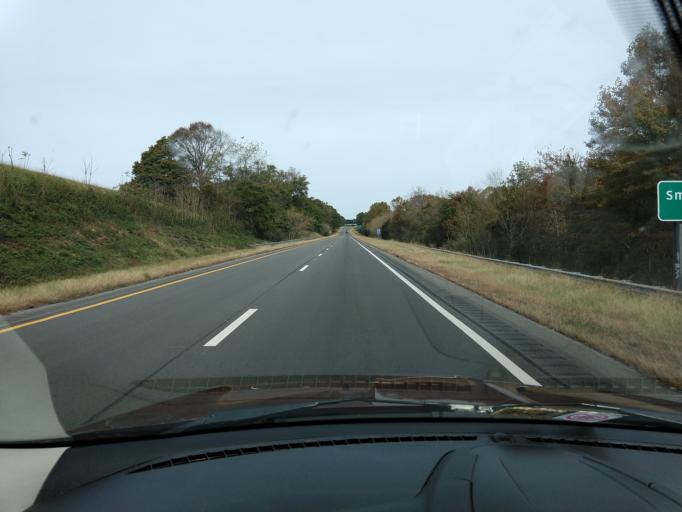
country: US
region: Virginia
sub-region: Pittsylvania County
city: Gretna
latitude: 36.9442
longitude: -79.3773
